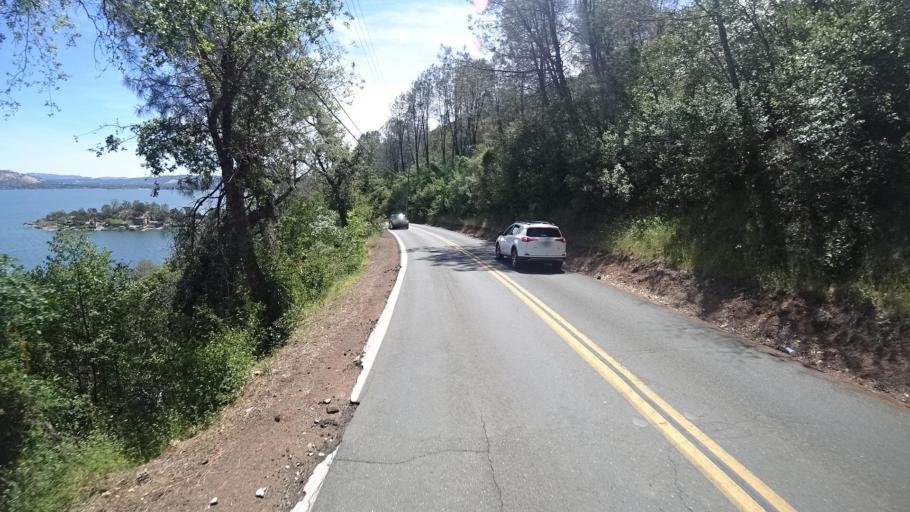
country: US
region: California
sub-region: Lake County
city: Clearlake
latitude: 38.9480
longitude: -122.6956
